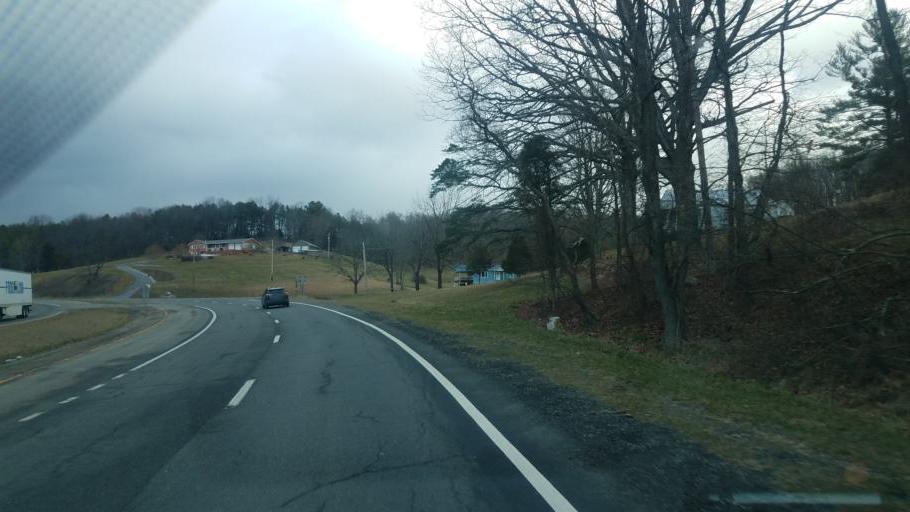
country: US
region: Virginia
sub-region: Giles County
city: Pearisburg
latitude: 37.2794
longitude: -80.7422
